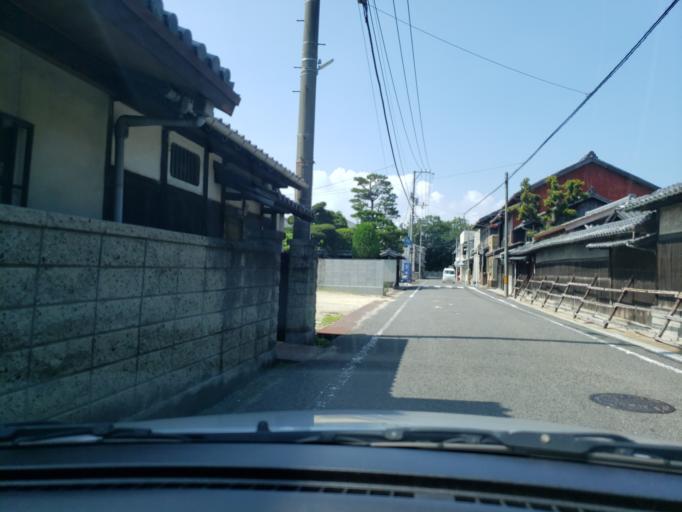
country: JP
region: Ehime
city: Hojo
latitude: 34.1073
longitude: 132.9675
